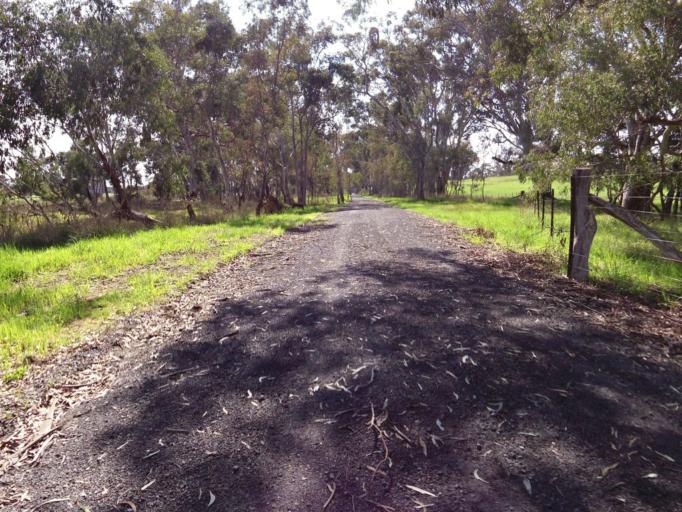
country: AU
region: Victoria
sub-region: Murrindindi
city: Alexandra
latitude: -37.1192
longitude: 145.6036
